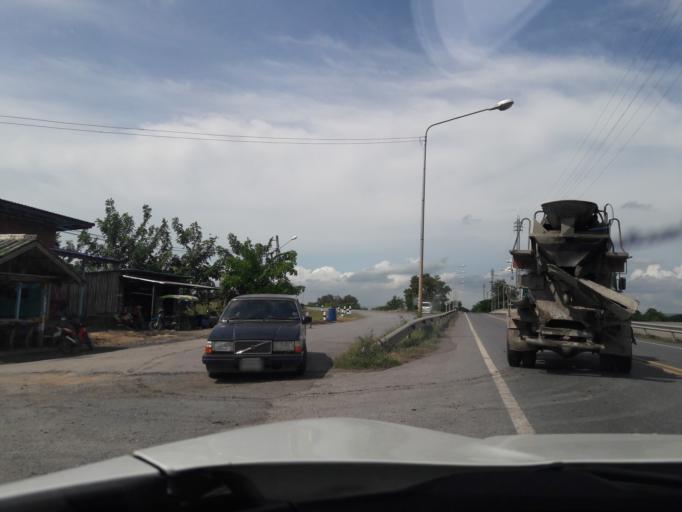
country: TH
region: Lop Buri
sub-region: Amphoe Tha Luang
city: Tha Luang
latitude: 15.0679
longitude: 101.0912
